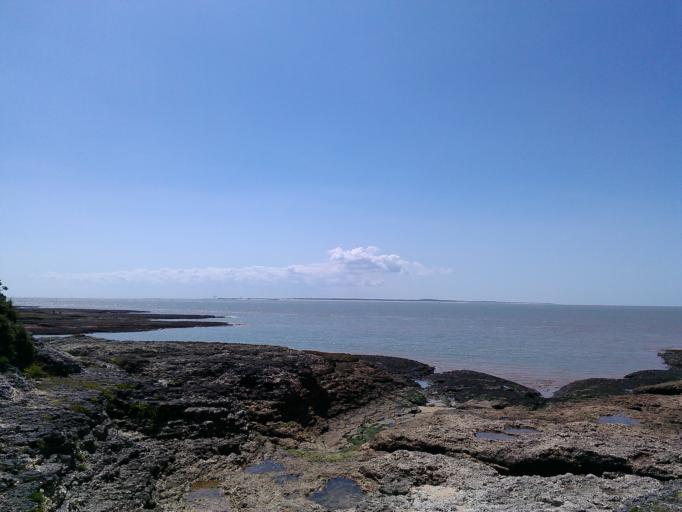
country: FR
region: Poitou-Charentes
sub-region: Departement de la Charente-Maritime
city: Saint-Palais-sur-Mer
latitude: 45.6346
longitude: -1.0722
